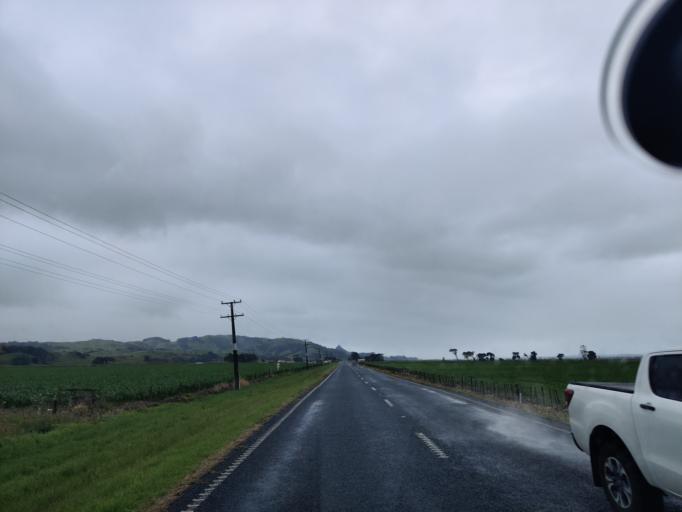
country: NZ
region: Northland
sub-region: Kaipara District
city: Dargaville
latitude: -36.0173
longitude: 173.9356
